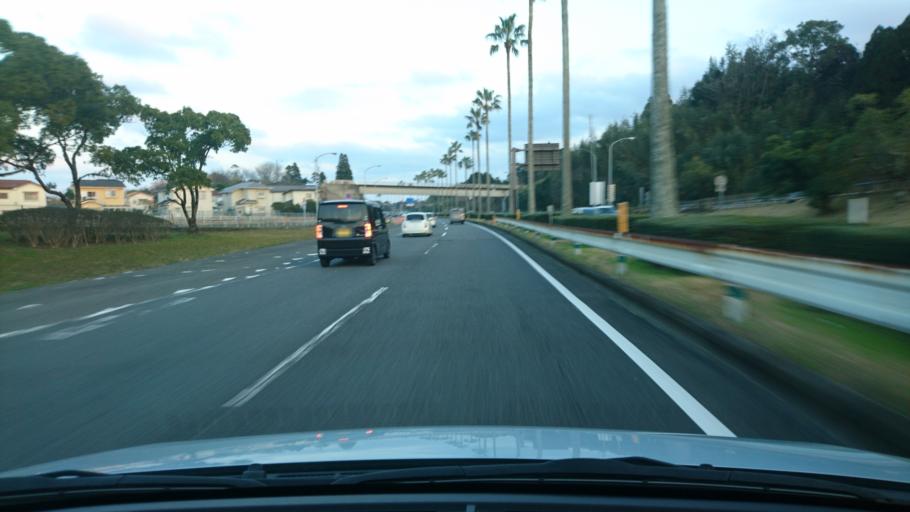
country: JP
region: Miyazaki
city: Miyazaki-shi
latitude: 31.8698
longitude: 131.4172
